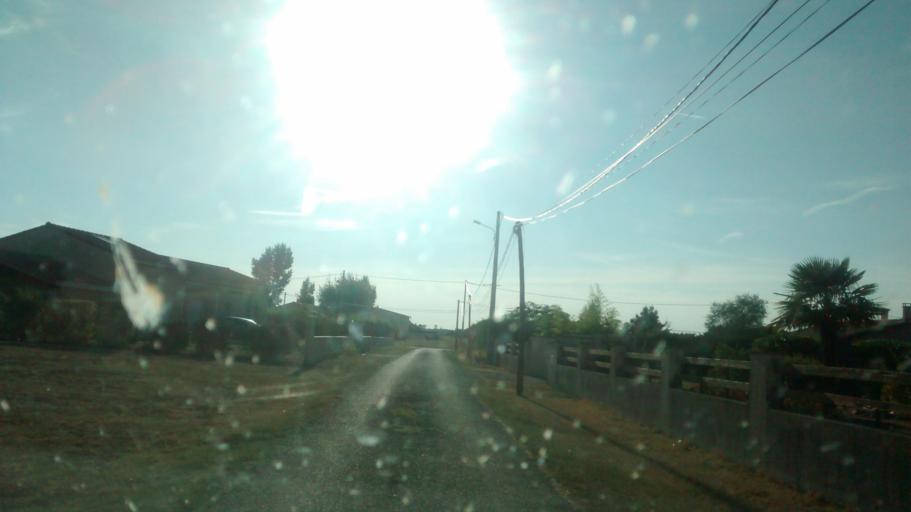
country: FR
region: Midi-Pyrenees
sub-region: Departement de la Haute-Garonne
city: Lherm
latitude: 43.4149
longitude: 1.2166
